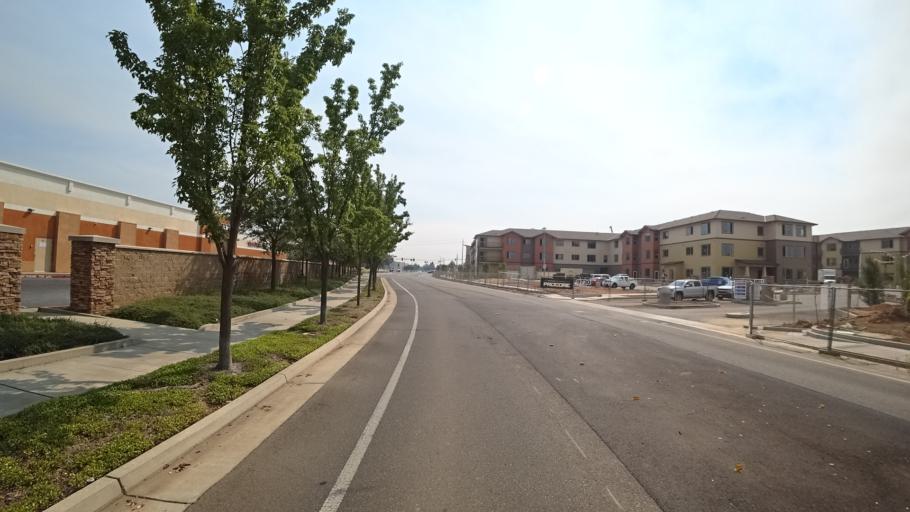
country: US
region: California
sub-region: Sacramento County
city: Laguna
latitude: 38.4051
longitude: -121.4197
